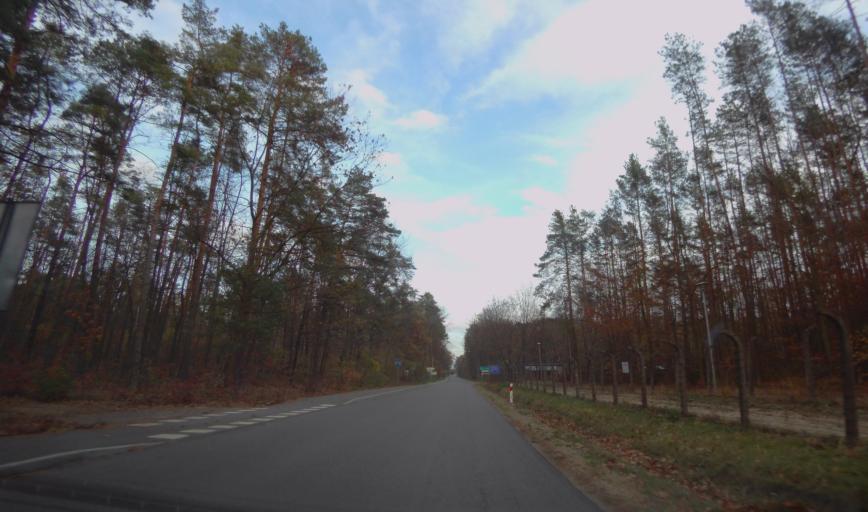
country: PL
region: Subcarpathian Voivodeship
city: Nowa Sarzyna
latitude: 50.3309
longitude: 22.3235
